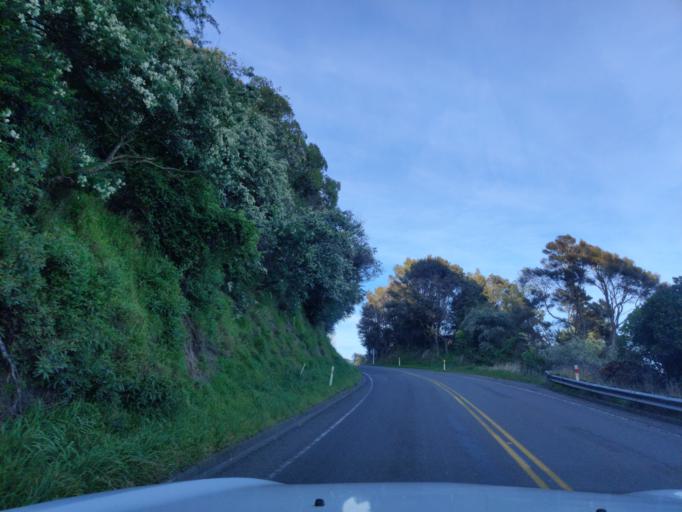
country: NZ
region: Manawatu-Wanganui
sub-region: Palmerston North City
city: Palmerston North
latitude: -40.2827
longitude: 175.7719
